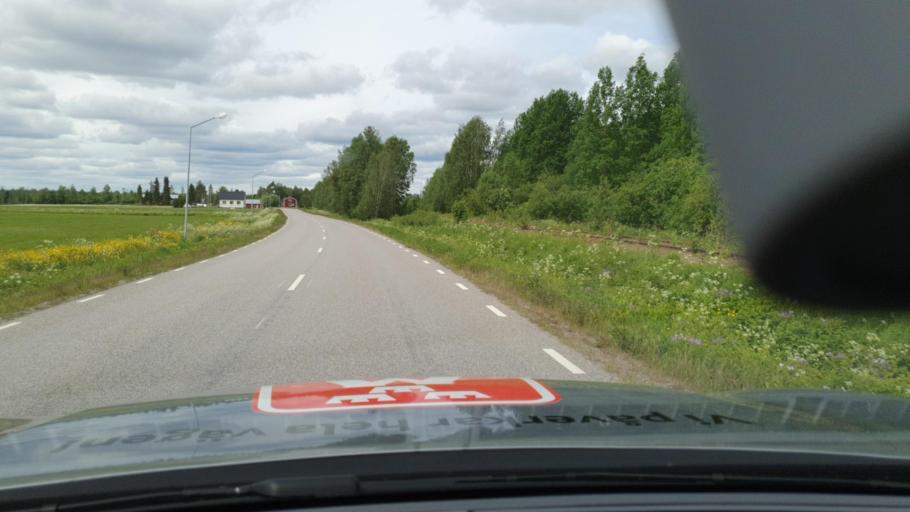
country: FI
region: Lapland
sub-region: Torniolaakso
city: Ylitornio
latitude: 66.0457
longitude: 23.6406
